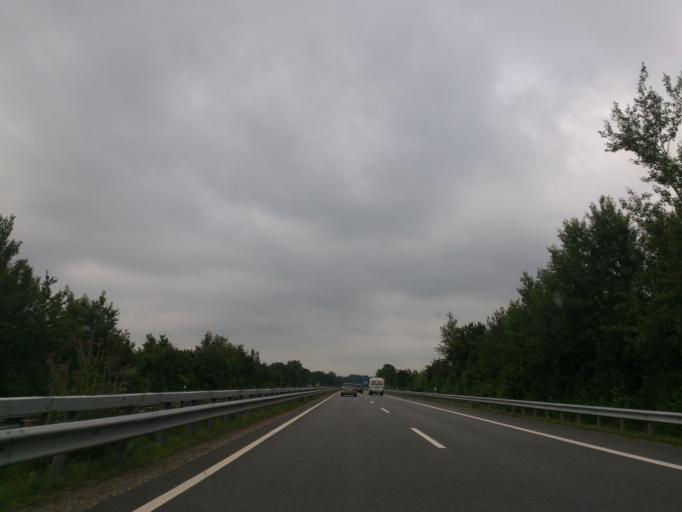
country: DE
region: Schleswig-Holstein
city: Ottenbuttel
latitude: 53.9704
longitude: 9.4918
